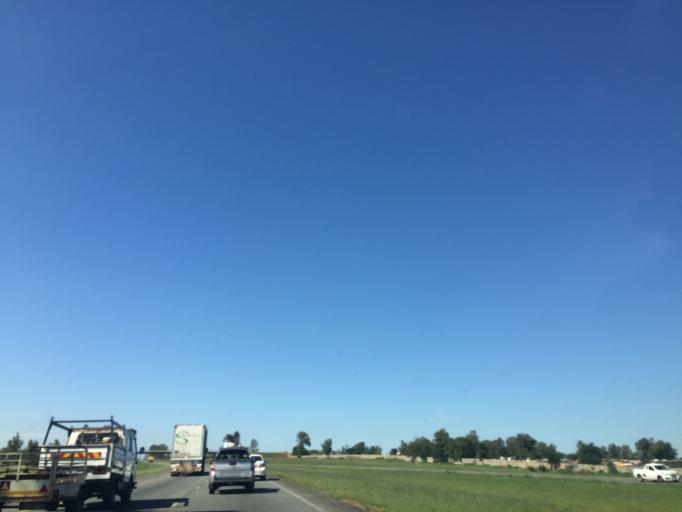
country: ZA
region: Gauteng
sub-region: Sedibeng District Municipality
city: Meyerton
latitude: -26.5410
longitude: 28.0099
